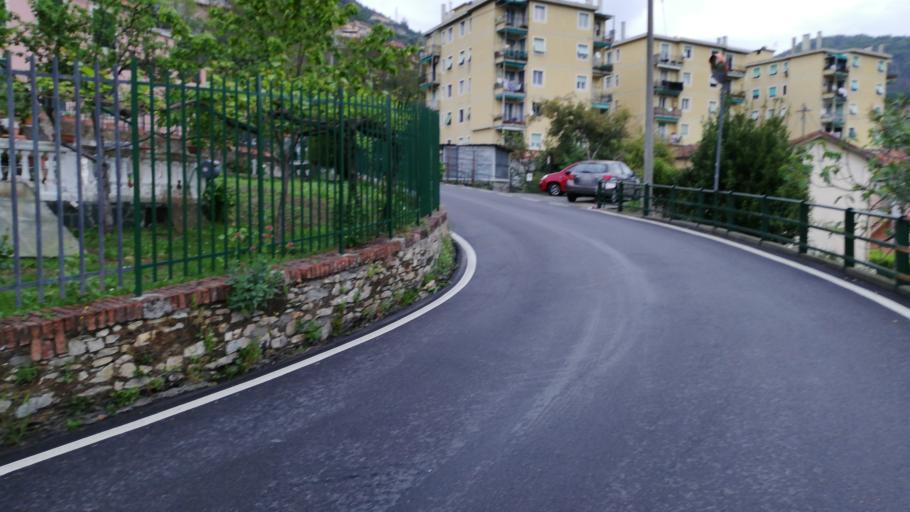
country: IT
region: Liguria
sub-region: Provincia di Genova
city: Piccarello
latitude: 44.4513
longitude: 9.0149
